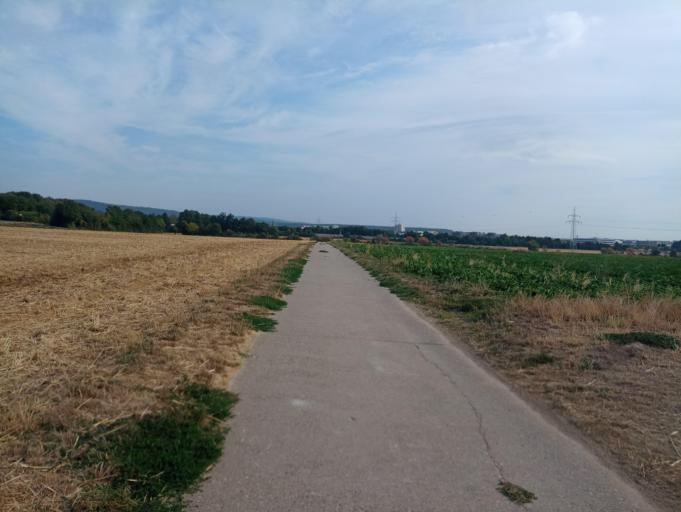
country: DE
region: Hesse
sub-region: Regierungsbezirk Darmstadt
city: Bad Homburg vor der Hoehe
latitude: 50.2062
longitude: 8.6041
